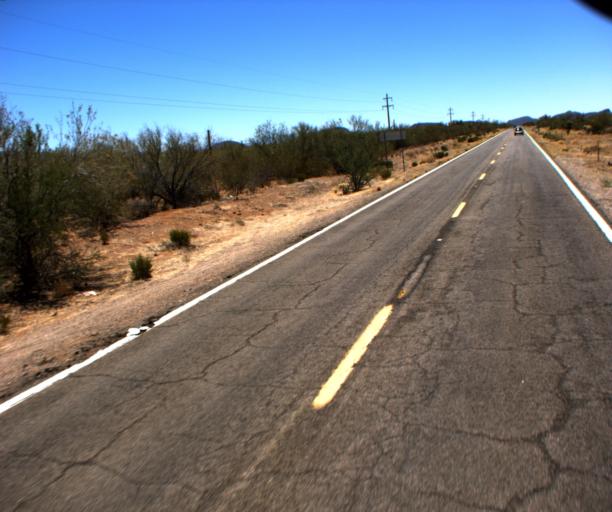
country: US
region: Arizona
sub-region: Pima County
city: Sells
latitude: 32.0312
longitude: -112.0102
